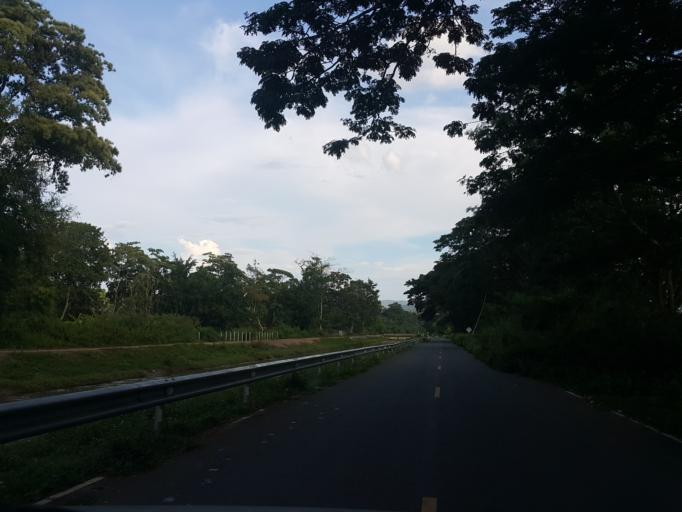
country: TH
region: Chiang Mai
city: Mae Taeng
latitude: 19.0601
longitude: 98.9671
